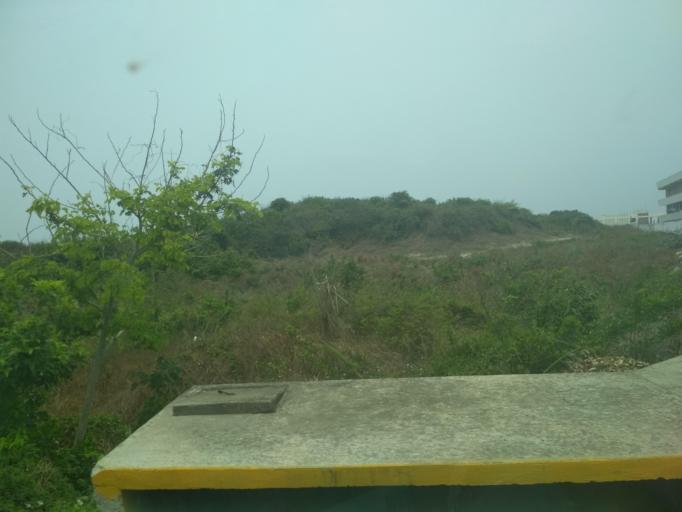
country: MX
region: Veracruz
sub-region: Alvarado
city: Playa de la Libertad
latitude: 19.0589
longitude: -96.0702
